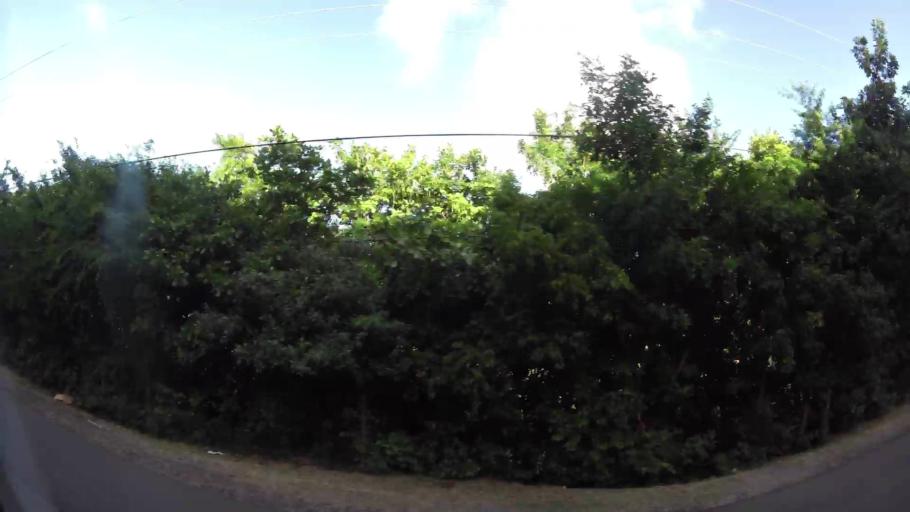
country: LC
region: Gros-Islet
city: Gros Islet
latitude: 14.1017
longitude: -60.9451
